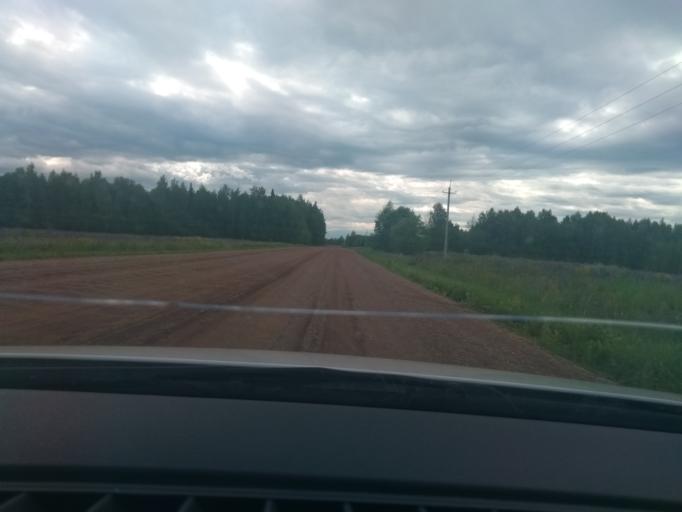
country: RU
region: Perm
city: Sylva
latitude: 57.8183
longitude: 56.7213
